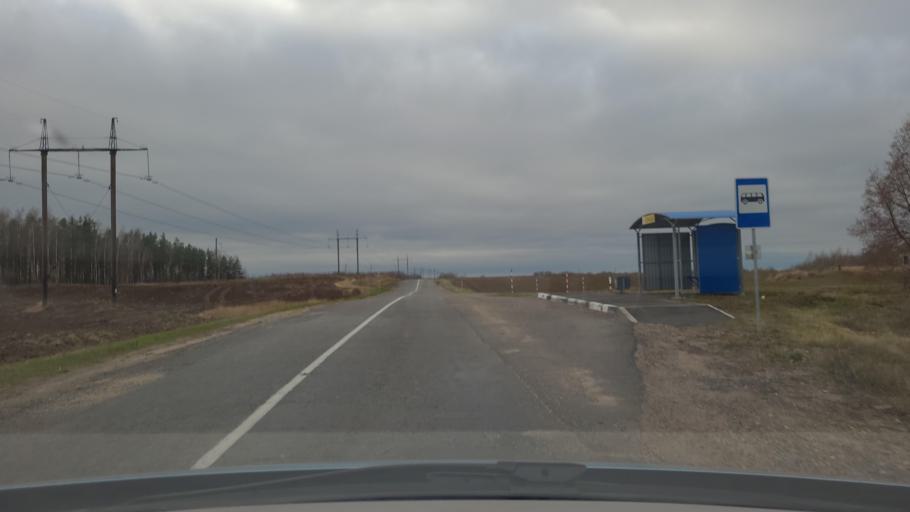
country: BY
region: Minsk
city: Khalopyenichy
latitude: 54.5540
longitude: 28.9889
